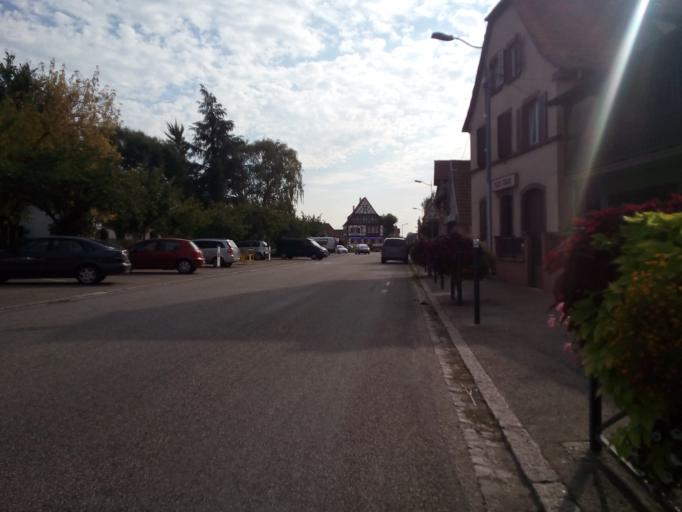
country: FR
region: Alsace
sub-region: Departement du Bas-Rhin
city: Herrlisheim
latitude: 48.7301
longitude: 7.9066
